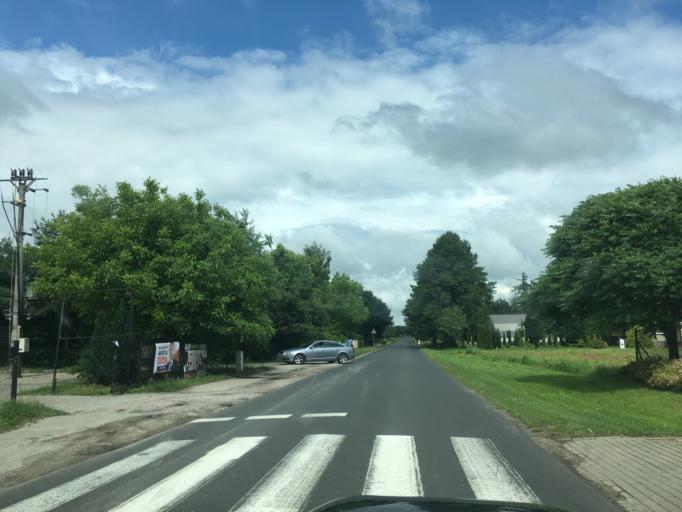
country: PL
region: Lublin Voivodeship
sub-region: Powiat swidnicki
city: Melgiew
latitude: 51.2080
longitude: 22.7419
